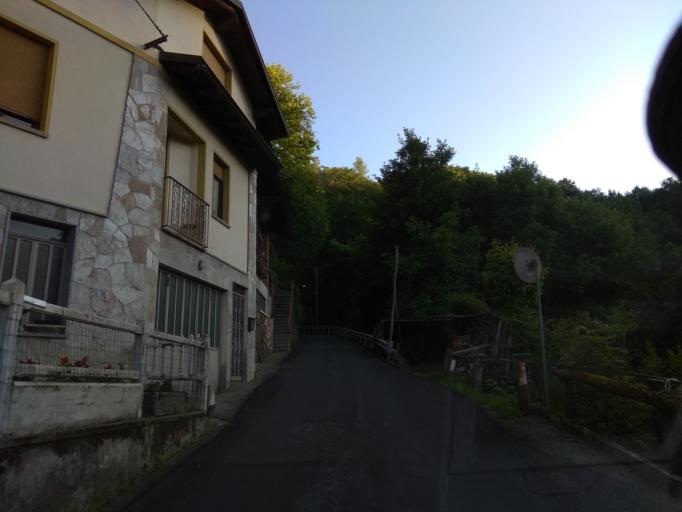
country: IT
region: Piedmont
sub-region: Provincia di Biella
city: Coggiola
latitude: 45.6996
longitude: 8.1820
